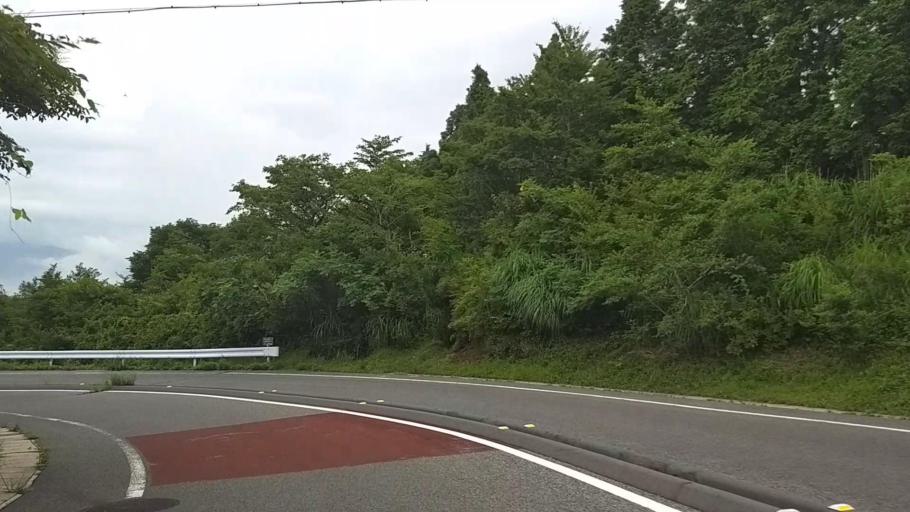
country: JP
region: Shizuoka
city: Gotemba
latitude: 35.3239
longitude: 139.0086
